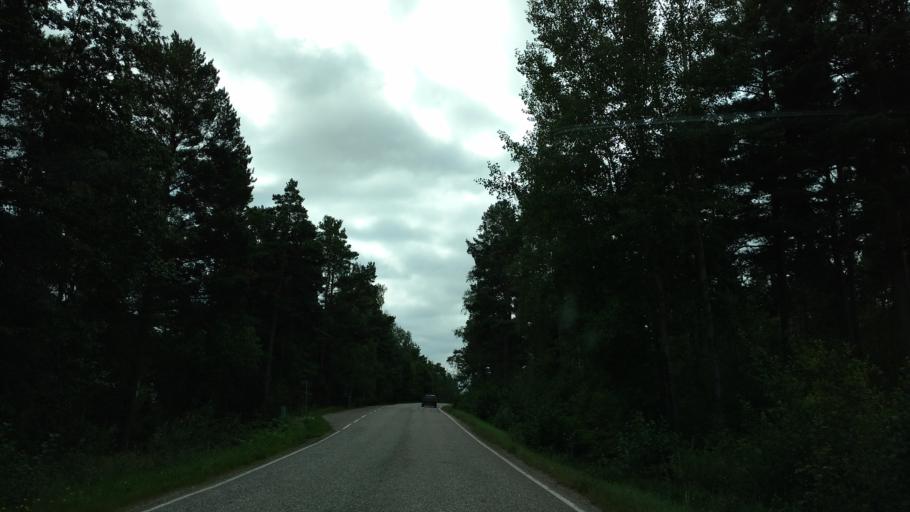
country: FI
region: Varsinais-Suomi
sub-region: Aboland-Turunmaa
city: Dragsfjaerd
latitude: 60.0025
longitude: 22.4537
